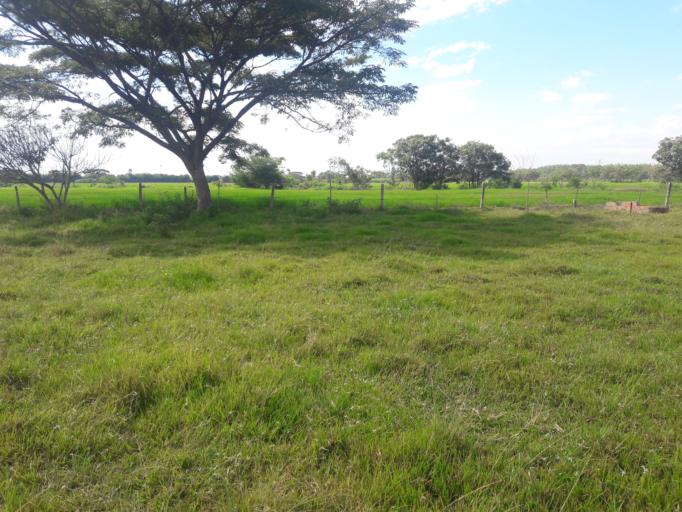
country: CO
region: Valle del Cauca
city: Jamundi
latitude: 3.2955
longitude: -76.5108
